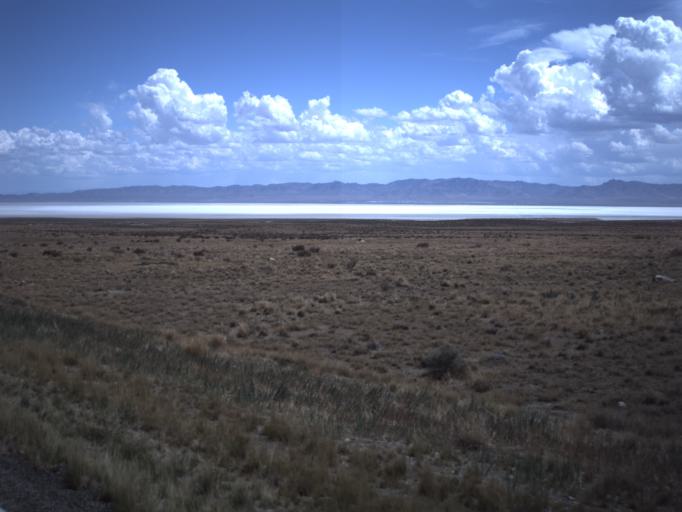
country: US
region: Utah
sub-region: Beaver County
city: Milford
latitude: 39.0531
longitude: -113.2653
